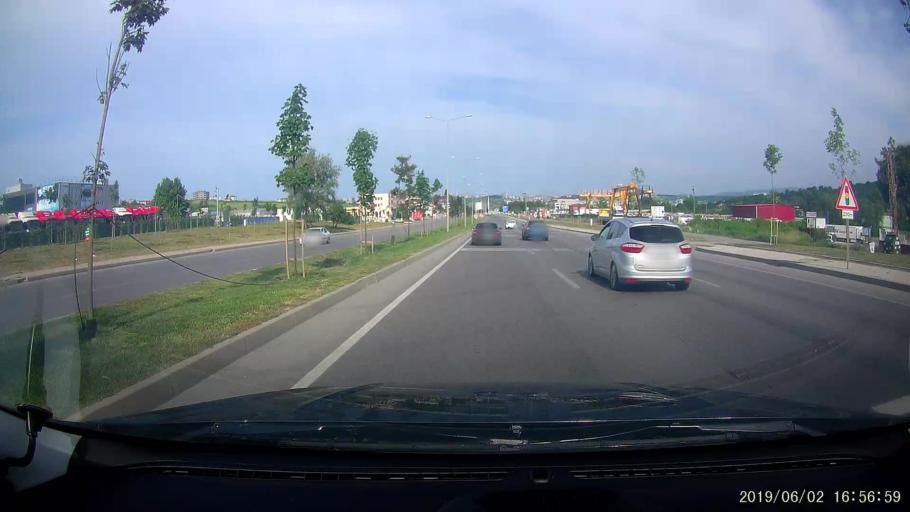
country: TR
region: Samsun
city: Samsun
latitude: 41.2916
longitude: 36.2690
